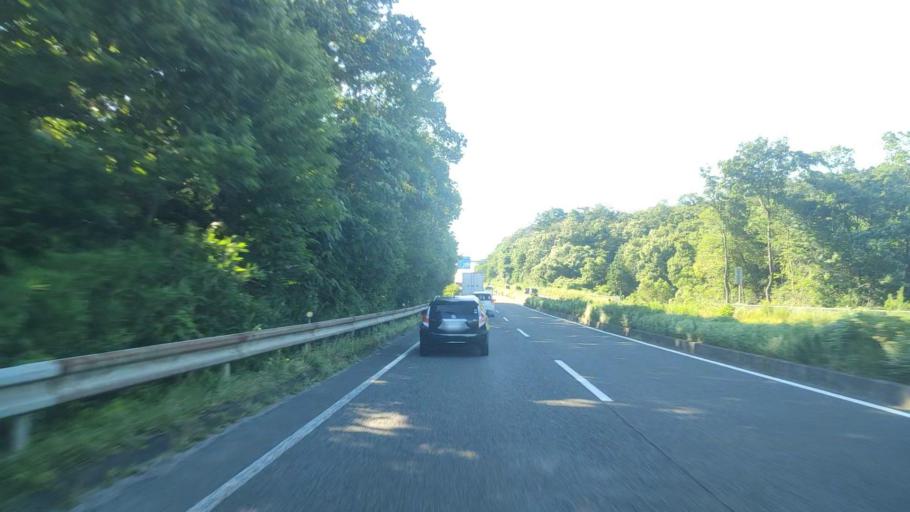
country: JP
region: Shiga Prefecture
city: Minakuchicho-matoba
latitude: 34.9686
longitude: 136.1941
